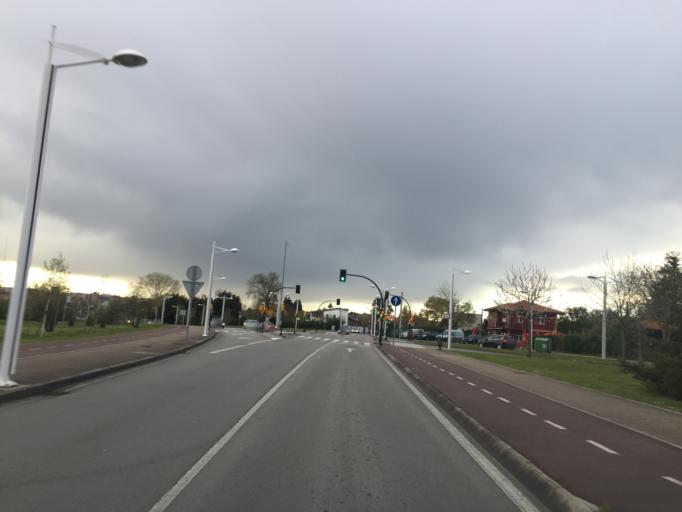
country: ES
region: Asturias
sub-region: Province of Asturias
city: Gijon
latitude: 43.5268
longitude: -5.6277
